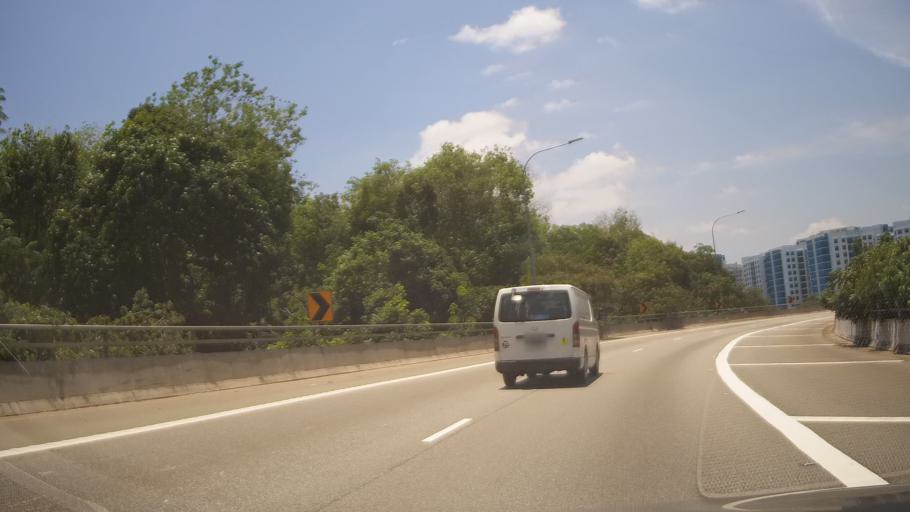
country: MY
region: Johor
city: Johor Bahru
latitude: 1.3909
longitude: 103.7759
